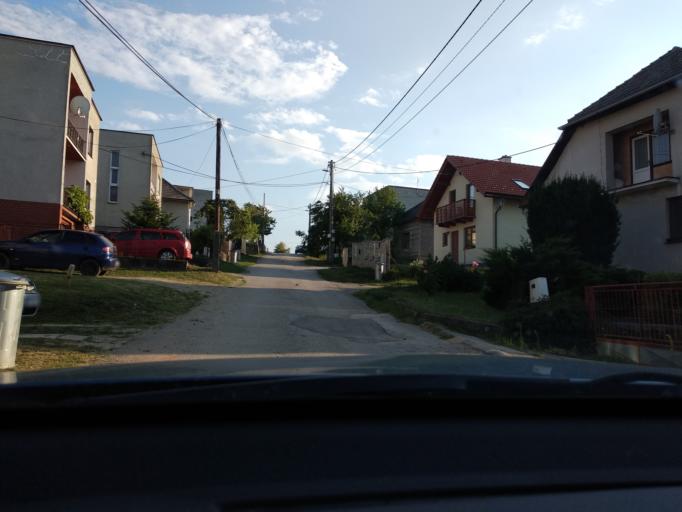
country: SK
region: Trenciansky
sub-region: Okres Trencin
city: Trencin
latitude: 48.8030
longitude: 18.1021
